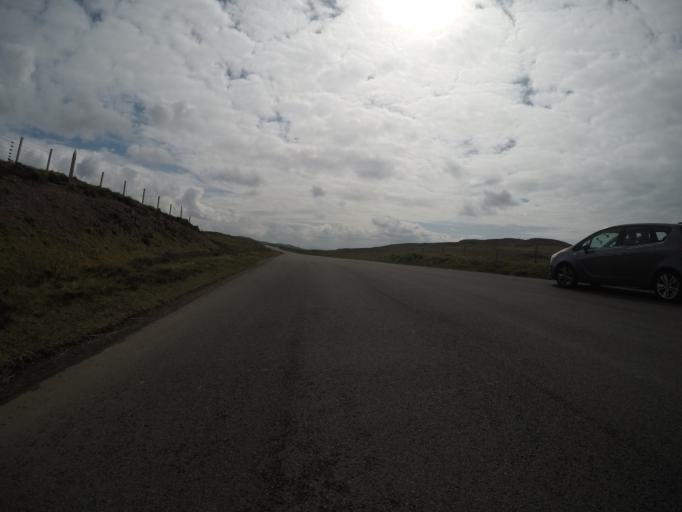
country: GB
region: Scotland
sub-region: Highland
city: Portree
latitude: 57.6020
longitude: -6.3778
